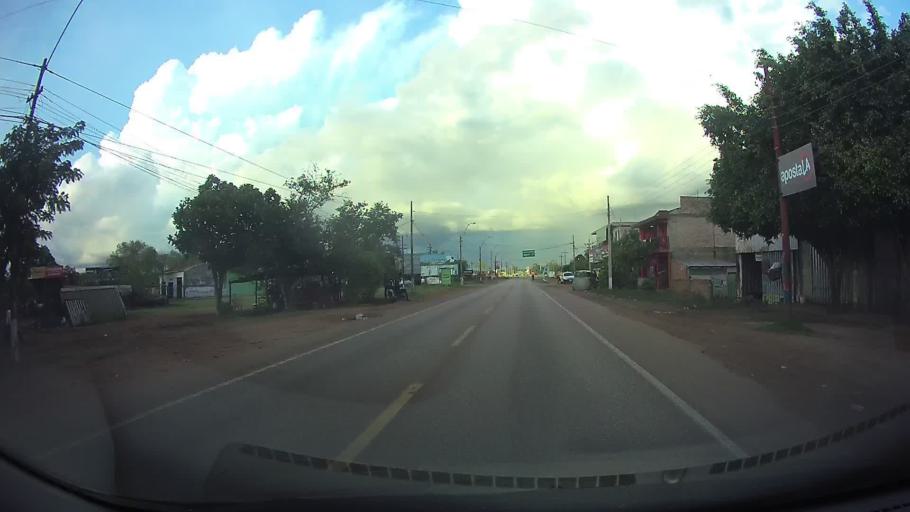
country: PY
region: Paraguari
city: Carapegua
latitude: -25.7660
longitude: -57.2365
